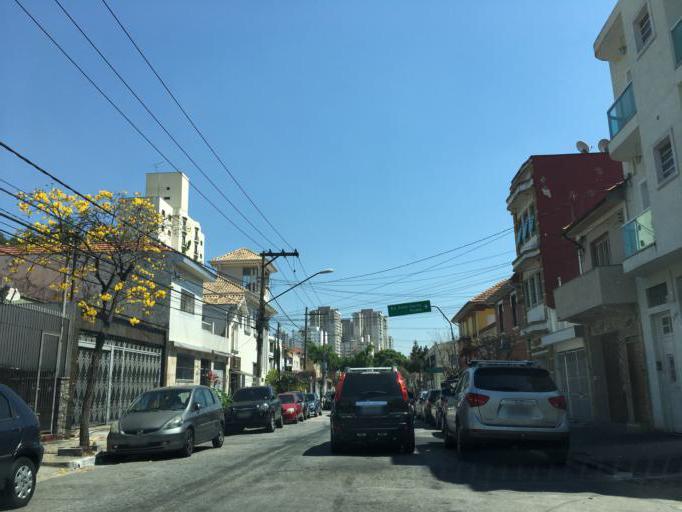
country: BR
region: Sao Paulo
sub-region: Sao Paulo
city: Sao Paulo
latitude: -23.5372
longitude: -46.5849
